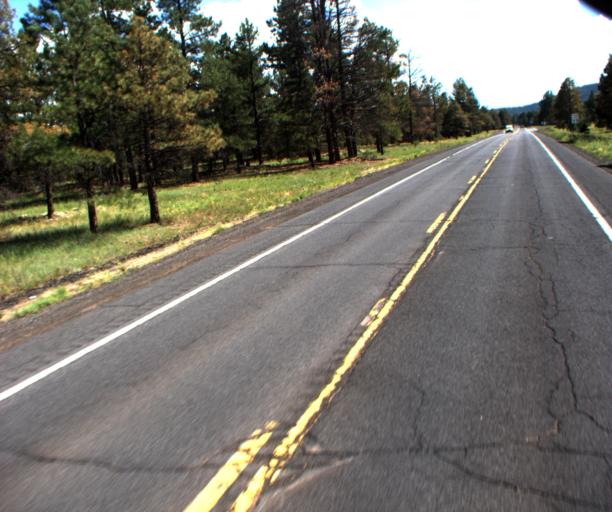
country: US
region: Arizona
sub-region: Coconino County
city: Williams
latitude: 35.2744
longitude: -112.1480
